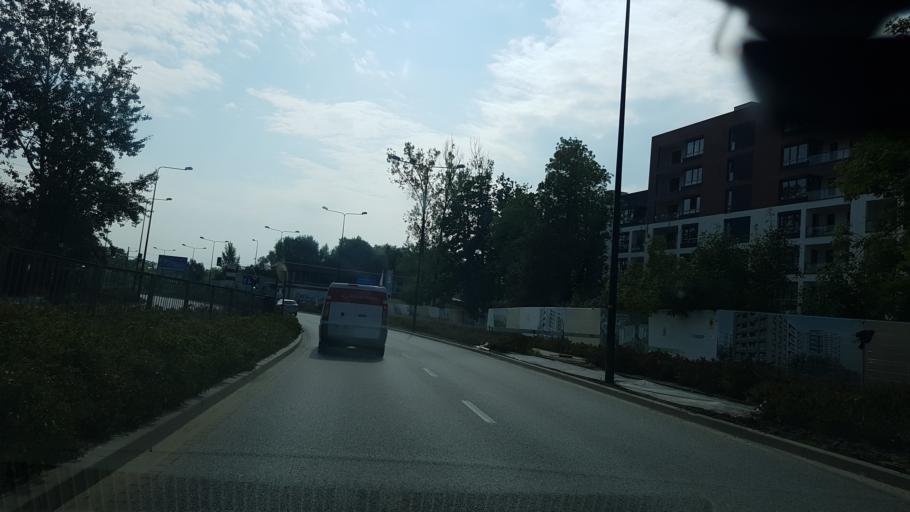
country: PL
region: Masovian Voivodeship
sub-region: Warszawa
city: Ursynow
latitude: 52.1688
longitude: 21.0419
